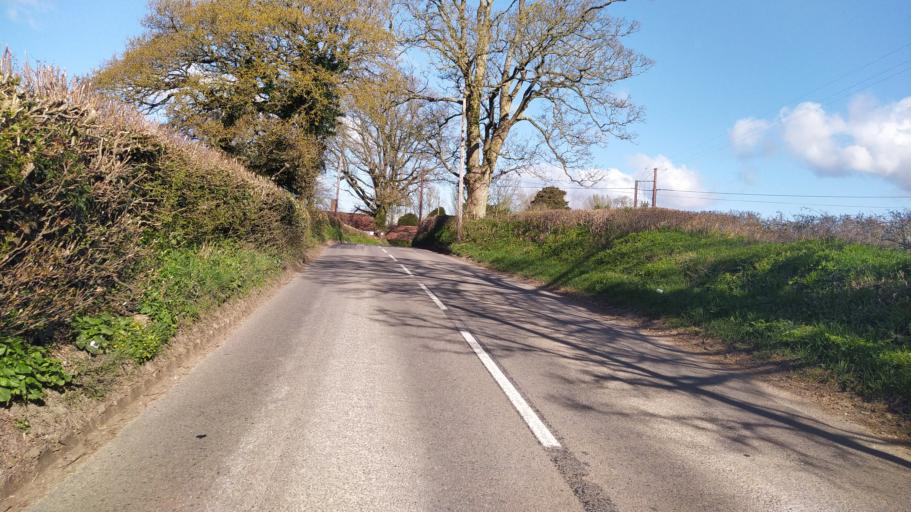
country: GB
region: England
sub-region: Dorset
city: Sturminster Newton
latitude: 50.9619
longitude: -2.3134
